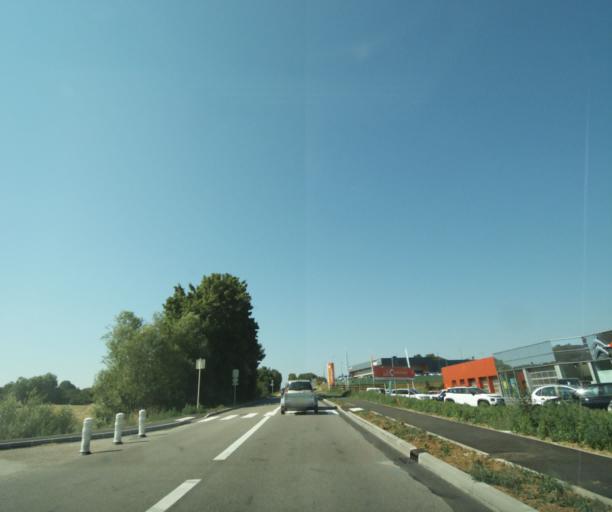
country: FR
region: Lorraine
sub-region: Departement de Meurthe-et-Moselle
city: Toul
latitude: 48.6630
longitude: 5.8790
